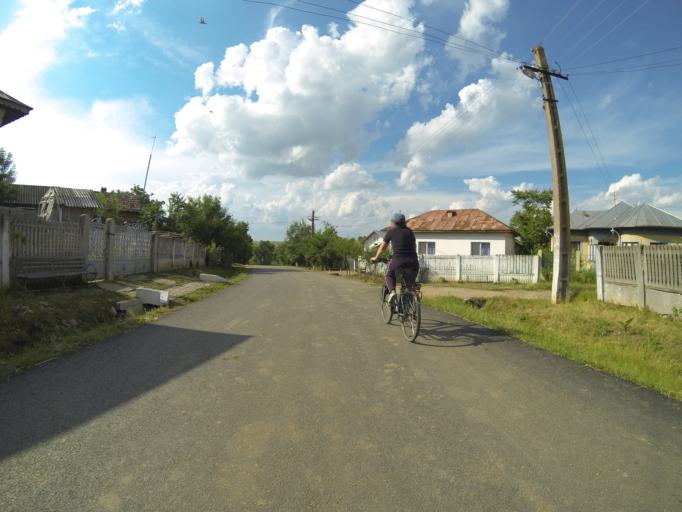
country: RO
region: Dolj
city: Satu Nou Calopar
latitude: 44.1304
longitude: 23.7930
